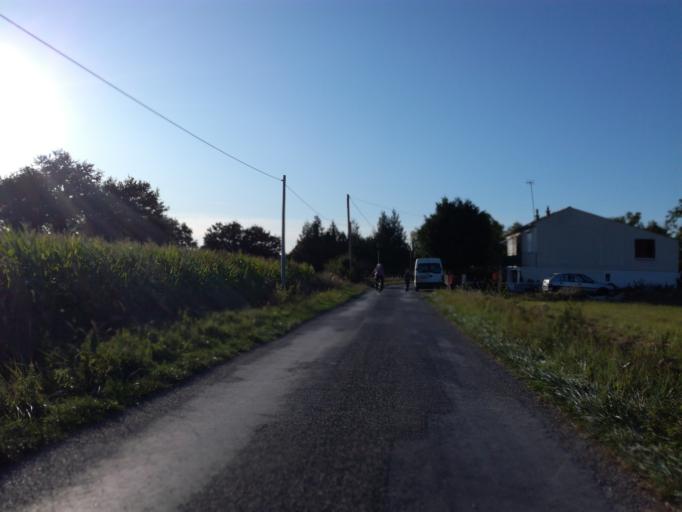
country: FR
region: Brittany
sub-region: Departement d'Ille-et-Vilaine
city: Betton
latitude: 48.1700
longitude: -1.6388
